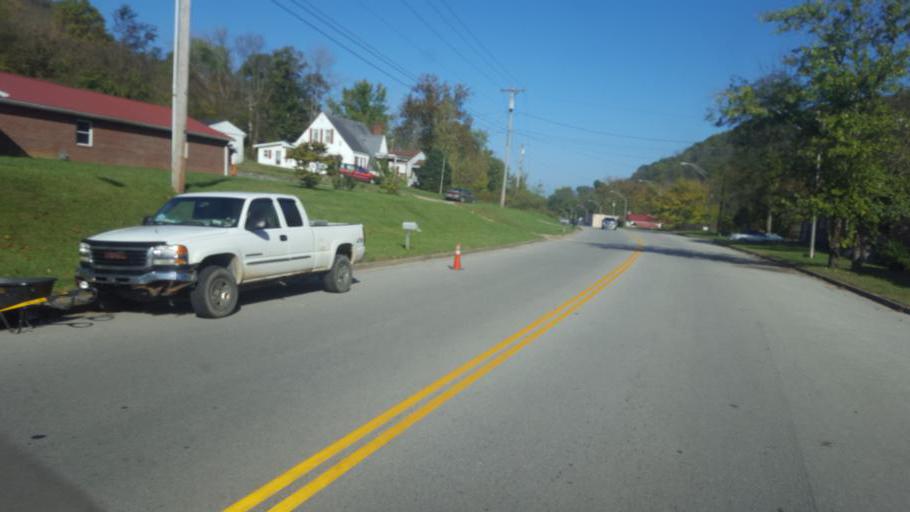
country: US
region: Kentucky
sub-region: Mason County
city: Maysville
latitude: 38.6302
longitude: -83.7504
